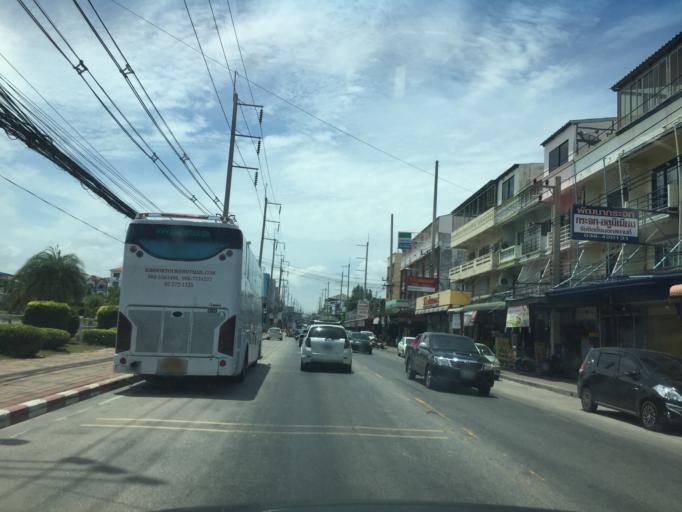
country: TH
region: Chon Buri
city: Phatthaya
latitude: 12.9219
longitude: 100.8859
